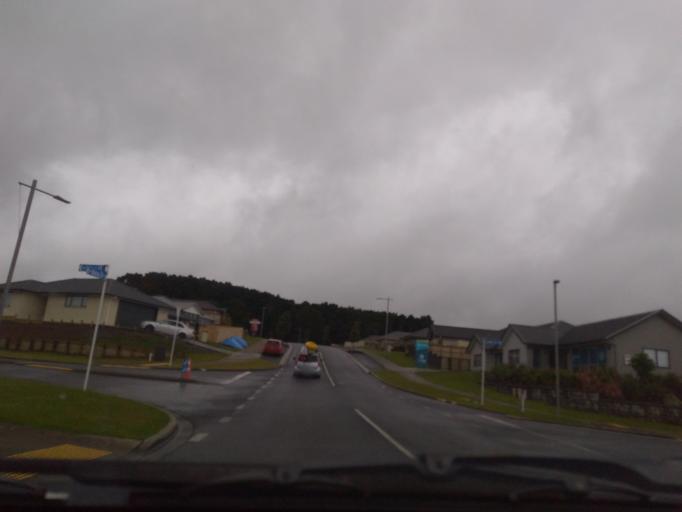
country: NZ
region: Northland
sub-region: Whangarei
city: Whangarei
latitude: -35.6777
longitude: 174.3165
